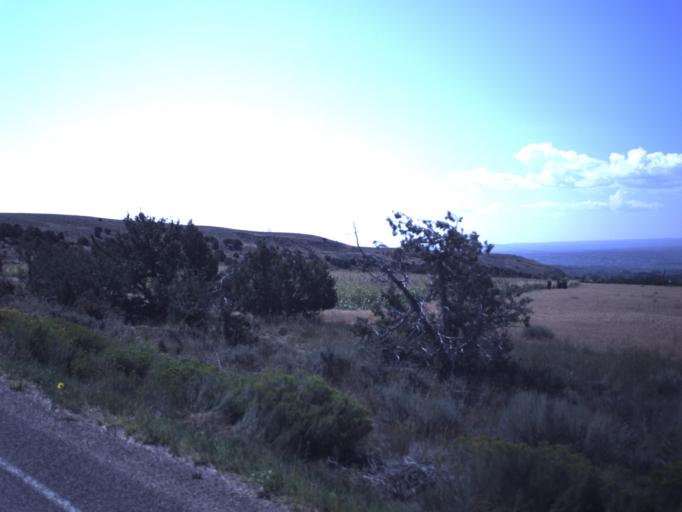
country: US
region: Utah
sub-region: Duchesne County
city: Duchesne
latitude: 40.2526
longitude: -110.3999
